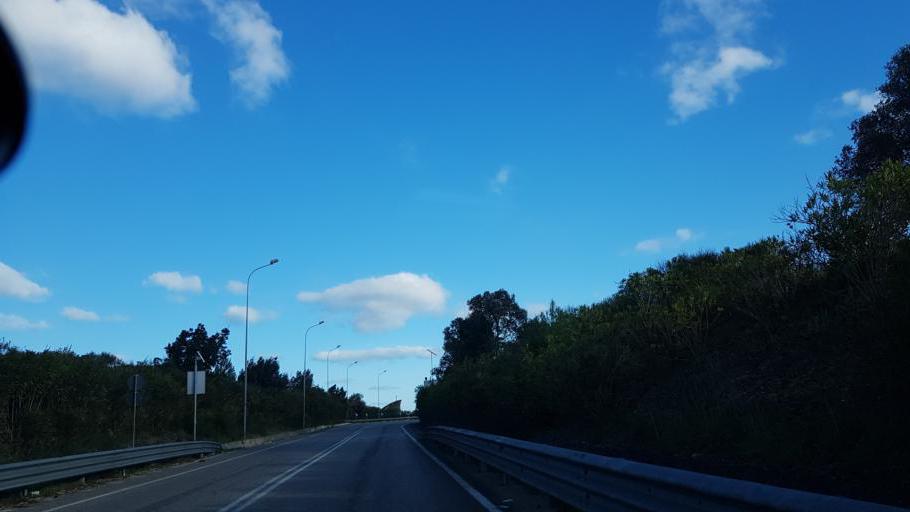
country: IT
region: Apulia
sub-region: Provincia di Brindisi
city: Brindisi
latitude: 40.6372
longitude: 17.9183
